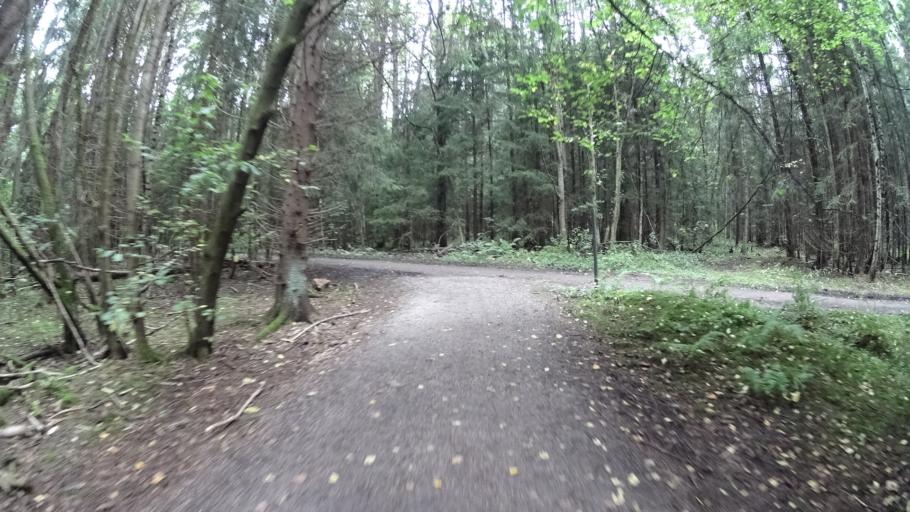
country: FI
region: Uusimaa
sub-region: Helsinki
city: Teekkarikylae
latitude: 60.2693
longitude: 24.8974
